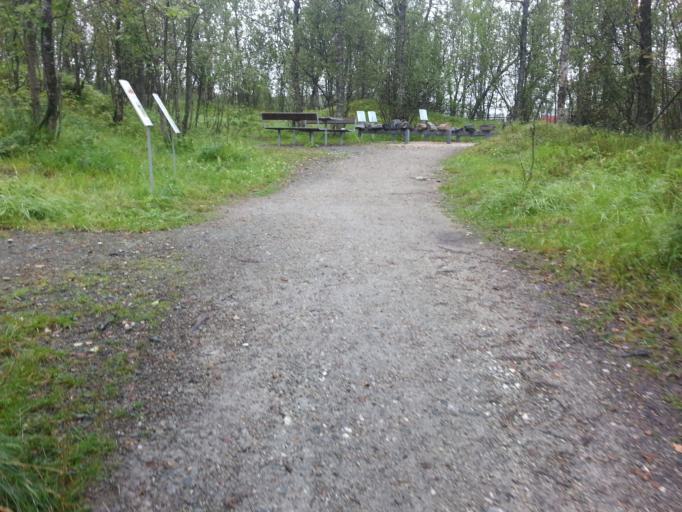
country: NO
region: Troms
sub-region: Tromso
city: Tromso
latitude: 69.6784
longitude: 18.9702
